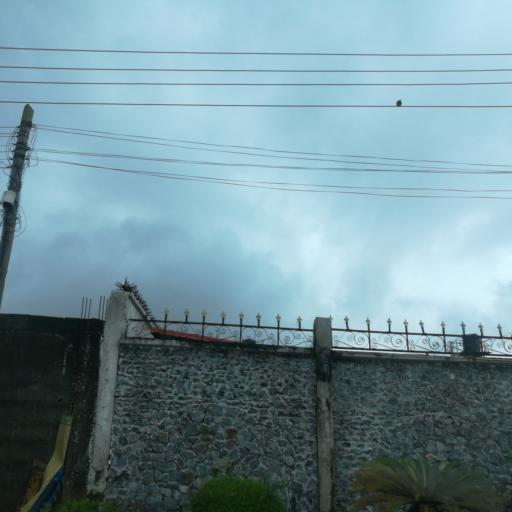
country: NG
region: Lagos
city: Ikoyi
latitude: 6.4389
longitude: 3.4624
